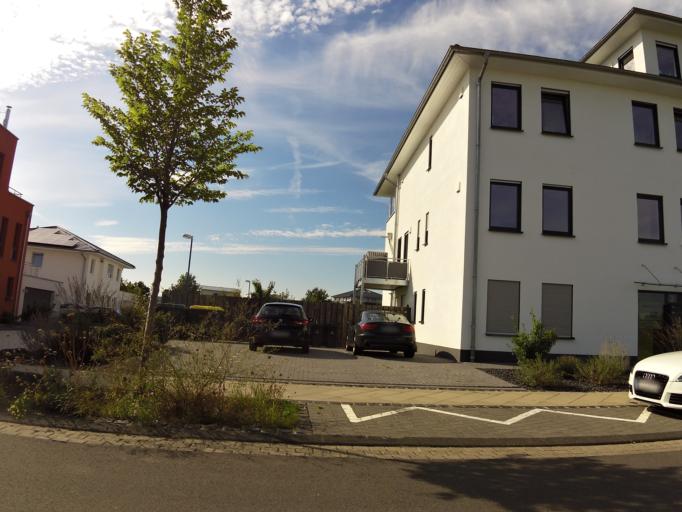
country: DE
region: North Rhine-Westphalia
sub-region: Regierungsbezirk Koln
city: Rheinbach
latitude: 50.6320
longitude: 6.9549
